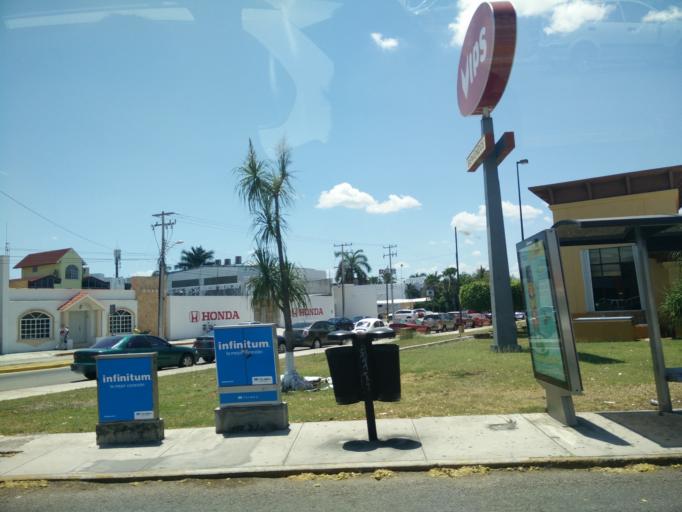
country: MX
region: Yucatan
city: Merida
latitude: 21.0249
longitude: -89.6233
